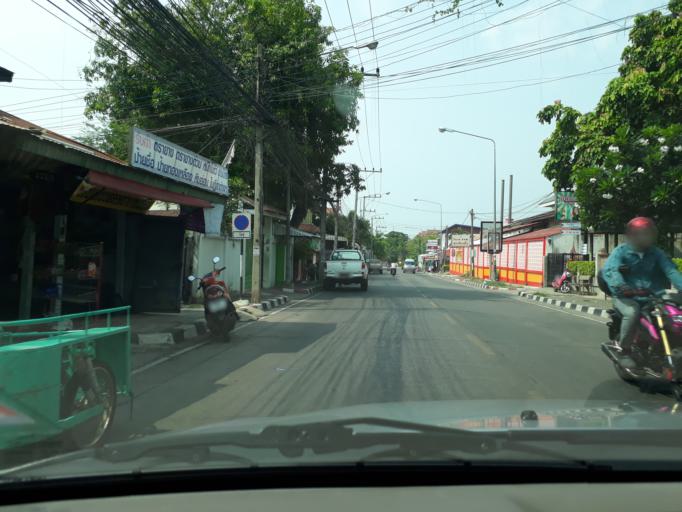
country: TH
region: Khon Kaen
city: Khon Kaen
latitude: 16.4257
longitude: 102.8367
